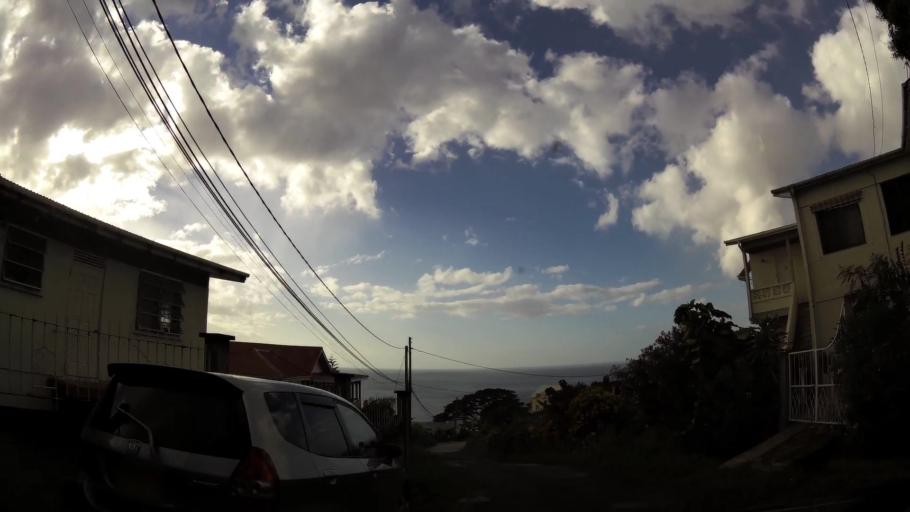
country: DM
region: Saint Paul
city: Mahaut
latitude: 15.3385
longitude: -61.3875
